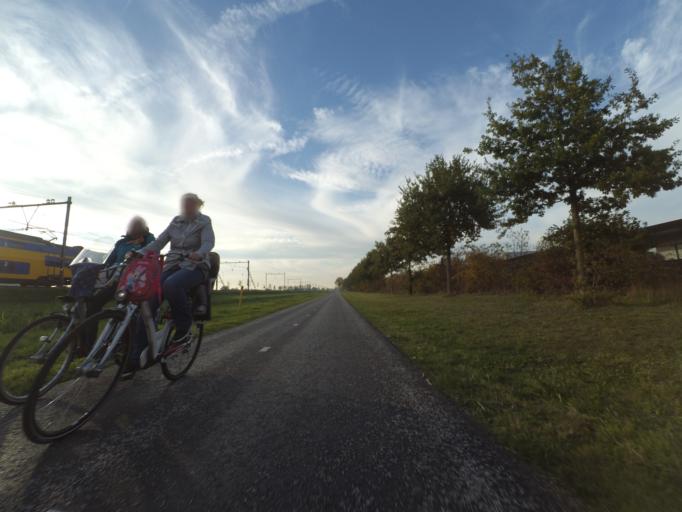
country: NL
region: Gelderland
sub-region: Gemeente Ede
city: Ederveen
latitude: 52.0392
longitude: 5.6119
